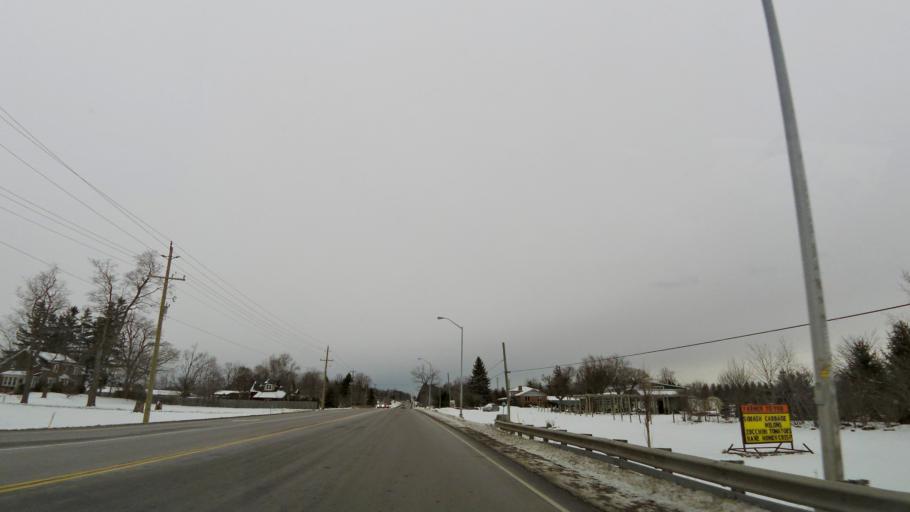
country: CA
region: Ontario
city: Ancaster
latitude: 43.2885
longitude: -80.0238
